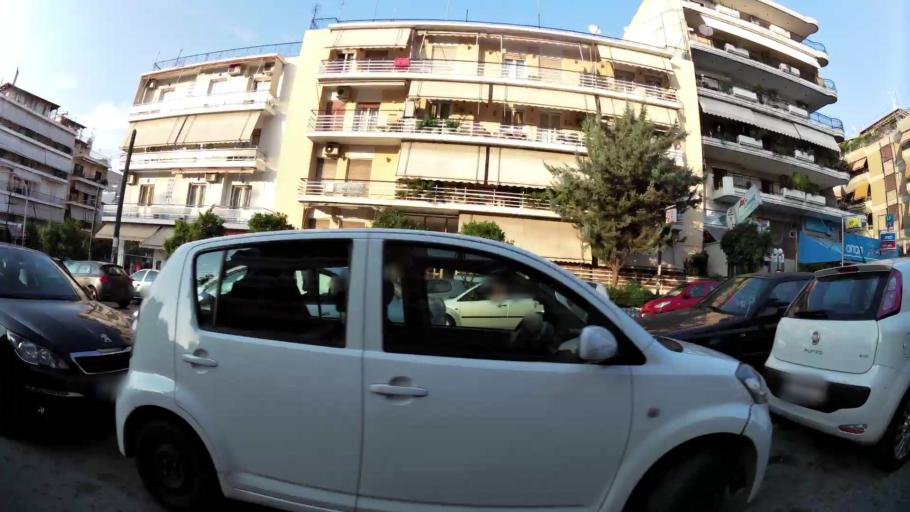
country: GR
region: Attica
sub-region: Nomarchia Athinas
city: Galatsi
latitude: 38.0197
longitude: 23.7534
